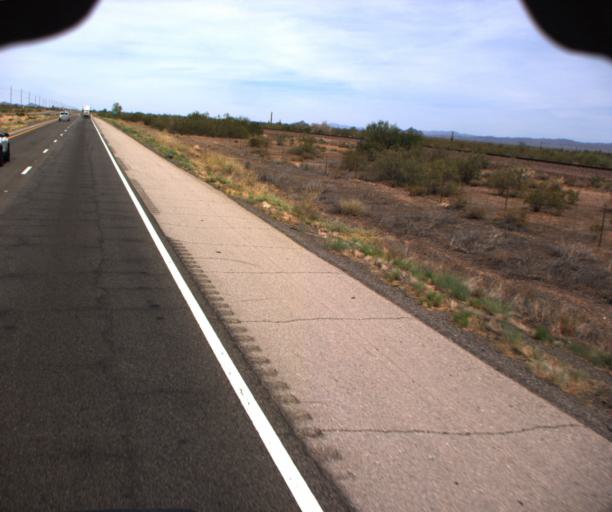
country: US
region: Arizona
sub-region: Maricopa County
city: Sun City West
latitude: 33.7929
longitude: -112.5477
